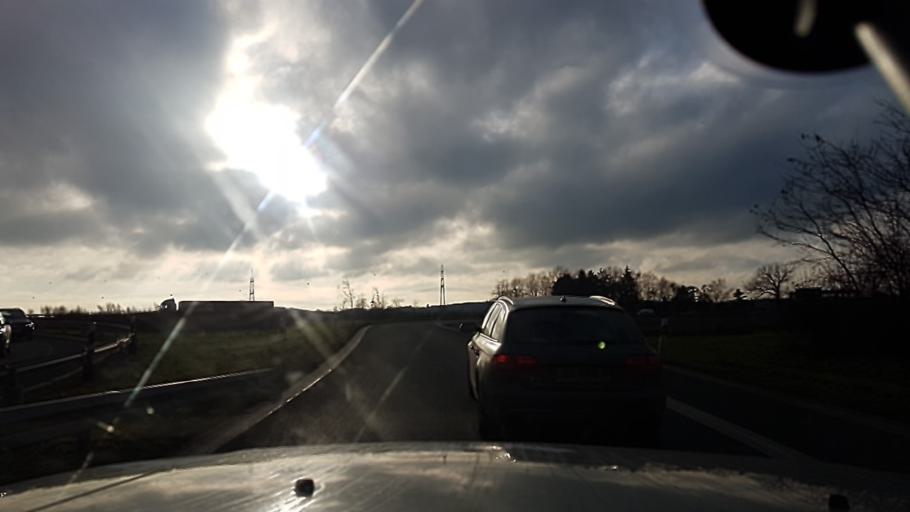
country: DE
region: North Rhine-Westphalia
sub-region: Regierungsbezirk Munster
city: Lotte
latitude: 52.2692
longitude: 7.9251
